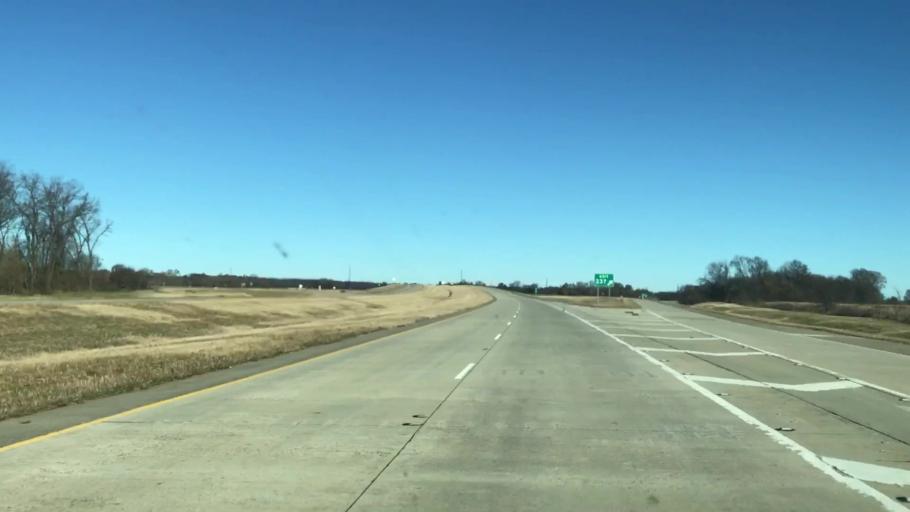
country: US
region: Louisiana
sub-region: Caddo Parish
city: Vivian
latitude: 32.8908
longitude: -93.8599
